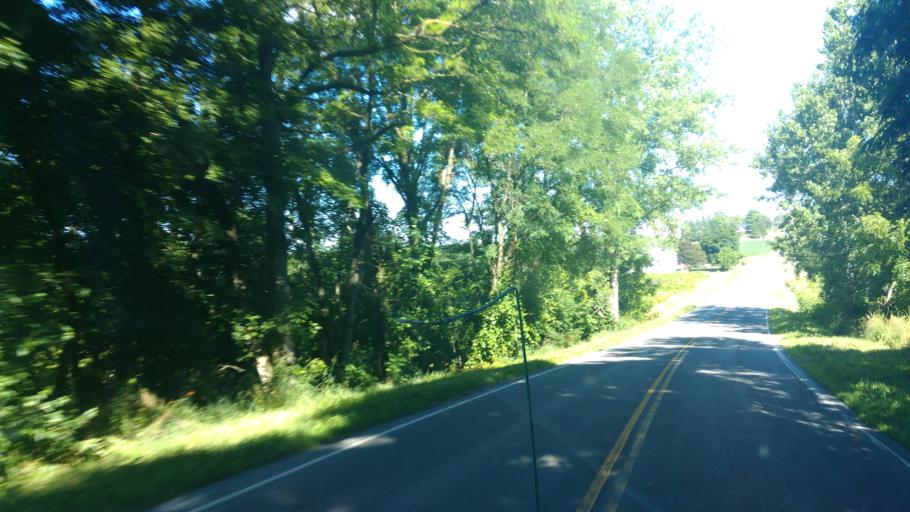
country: US
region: New York
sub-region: Wayne County
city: Clyde
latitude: 43.0232
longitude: -76.8220
